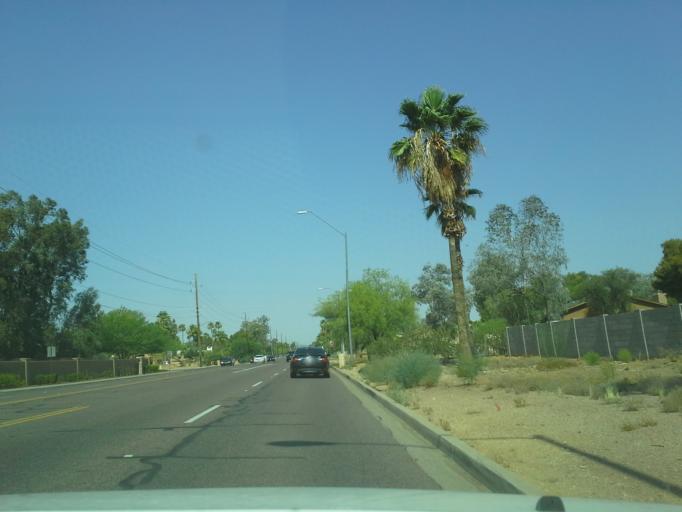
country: US
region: Arizona
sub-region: Maricopa County
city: Paradise Valley
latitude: 33.5970
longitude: -111.9506
